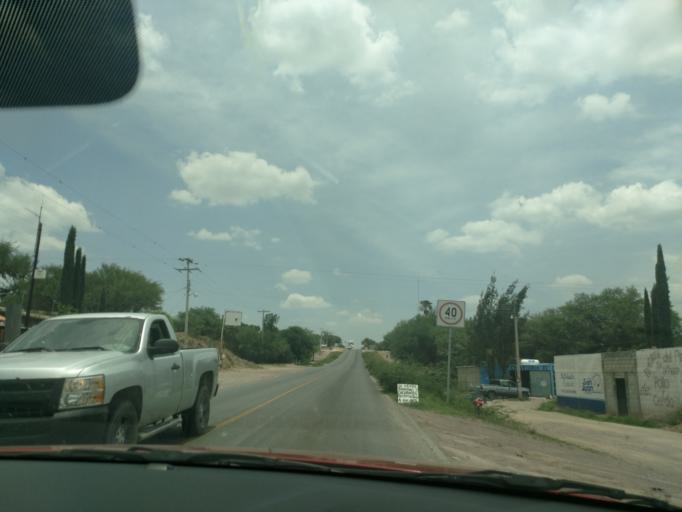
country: MX
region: San Luis Potosi
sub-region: Rioverde
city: Progreso
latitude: 22.0190
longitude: -100.3754
